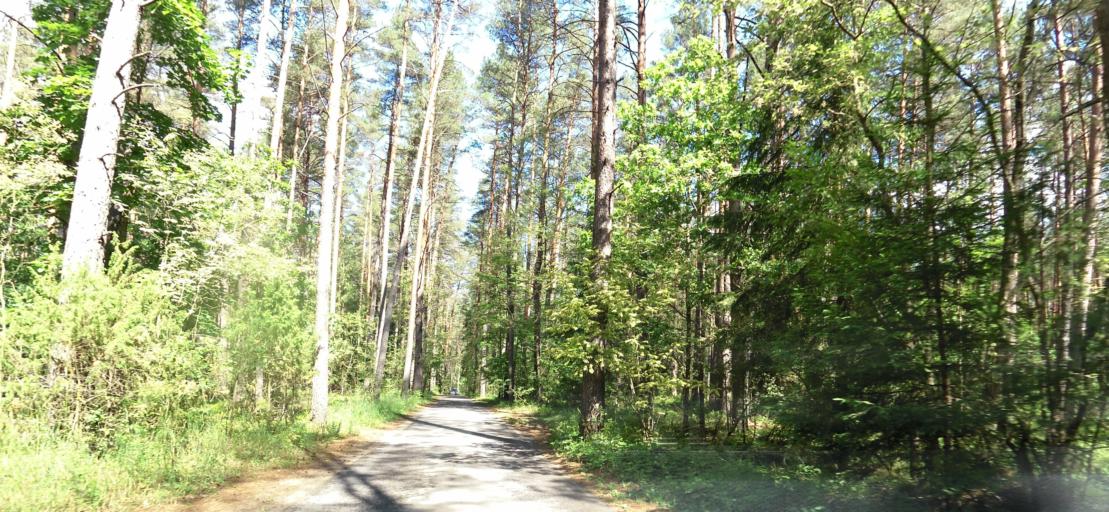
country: LT
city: Nemencine
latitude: 54.8093
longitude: 25.3944
